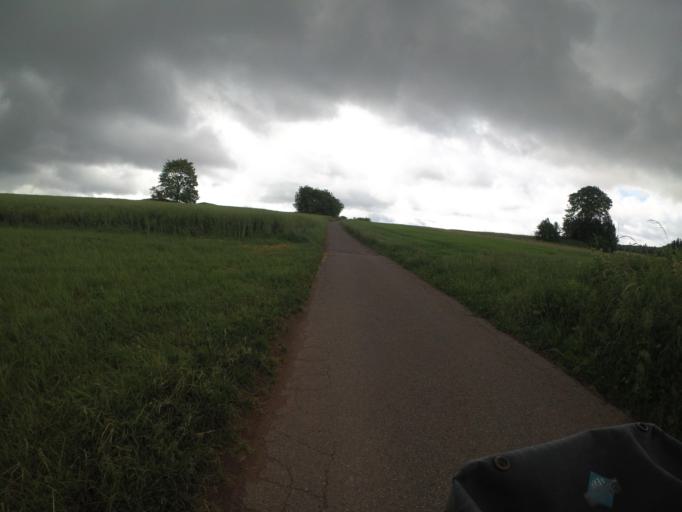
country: DE
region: Rheinland-Pfalz
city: Obersimten
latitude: 49.1640
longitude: 7.6034
